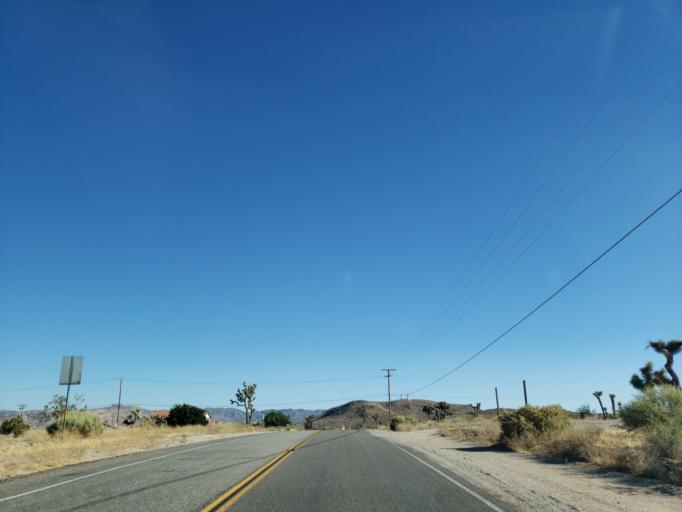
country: US
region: California
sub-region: San Bernardino County
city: Yucca Valley
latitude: 34.1722
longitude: -116.3871
